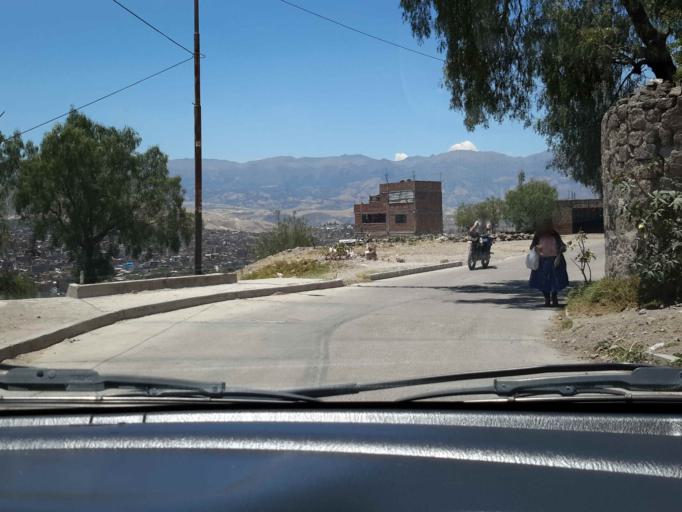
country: PE
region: Ayacucho
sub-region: Provincia de Huamanga
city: Ayacucho
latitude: -13.1697
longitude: -74.2240
